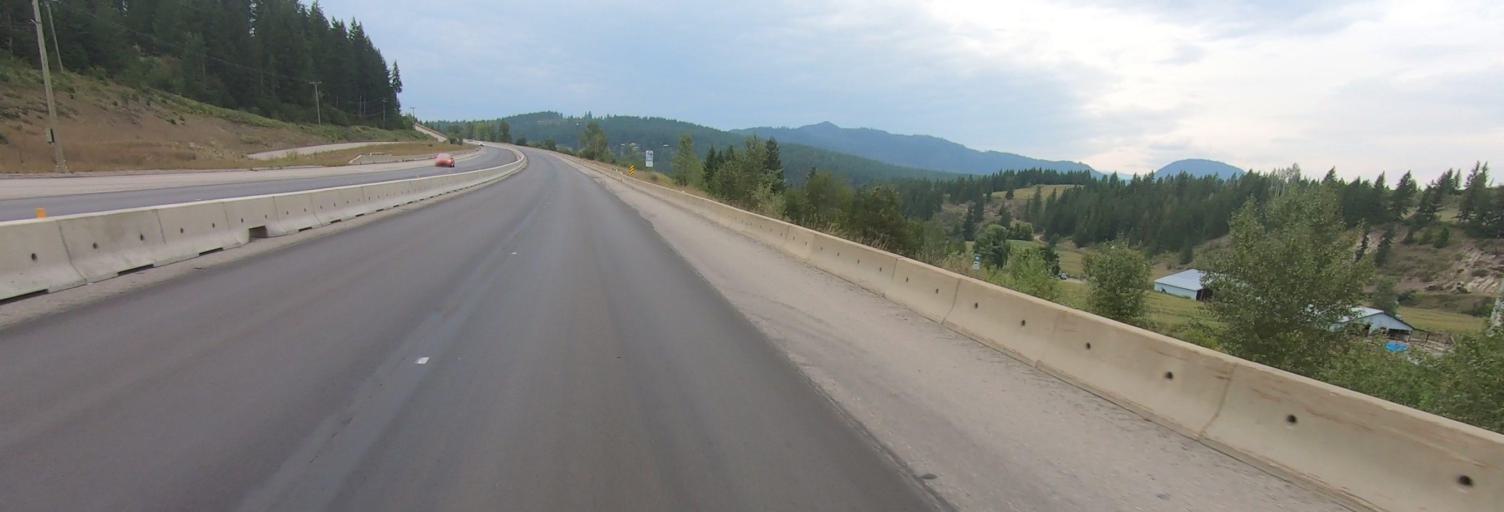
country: CA
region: British Columbia
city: Salmon Arm
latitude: 50.8406
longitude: -119.3284
